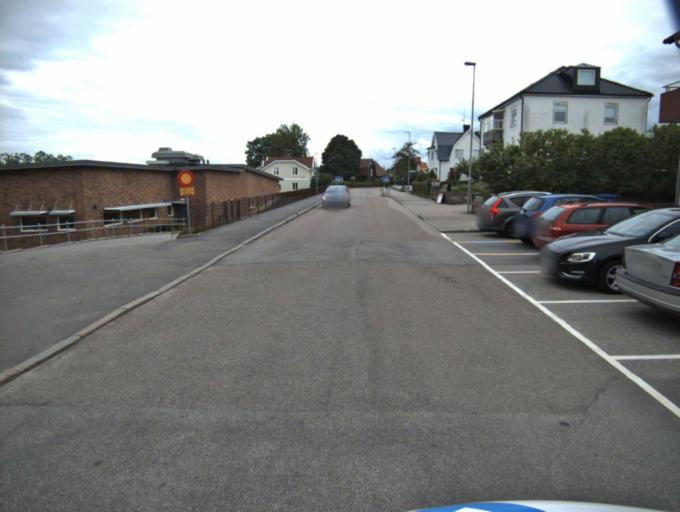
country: SE
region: Vaestra Goetaland
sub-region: Ulricehamns Kommun
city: Ulricehamn
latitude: 57.7935
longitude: 13.4193
